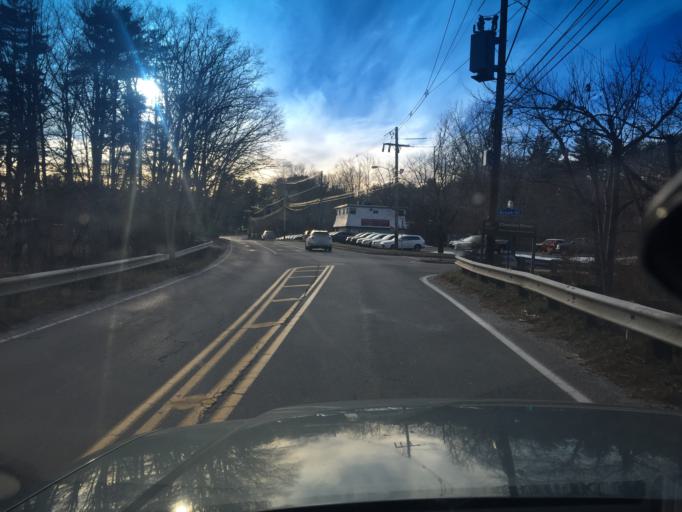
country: US
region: Massachusetts
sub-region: Middlesex County
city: Holliston
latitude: 42.2184
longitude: -71.4102
